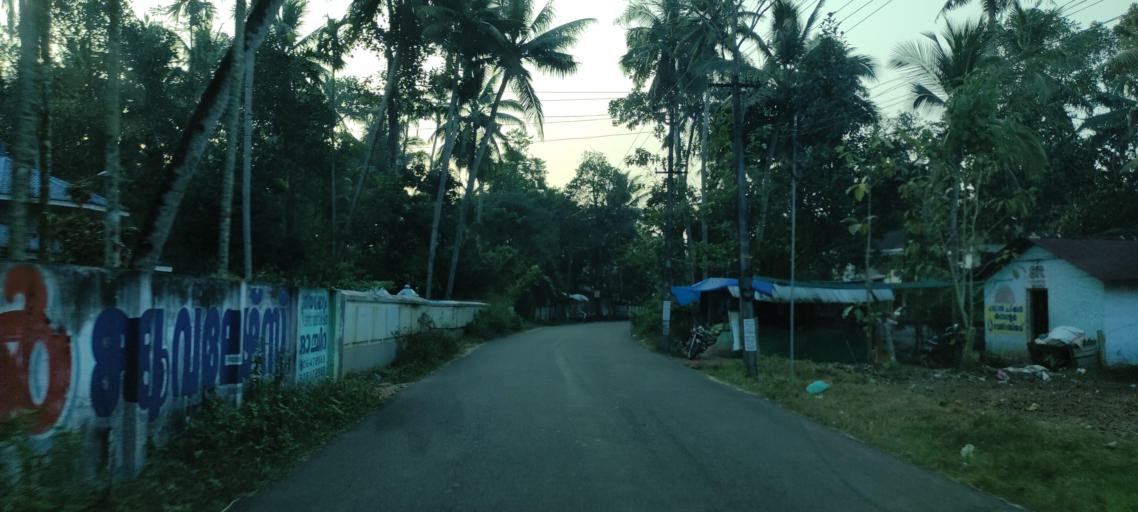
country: IN
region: Kerala
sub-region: Alappuzha
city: Kayankulam
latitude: 9.1350
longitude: 76.5292
